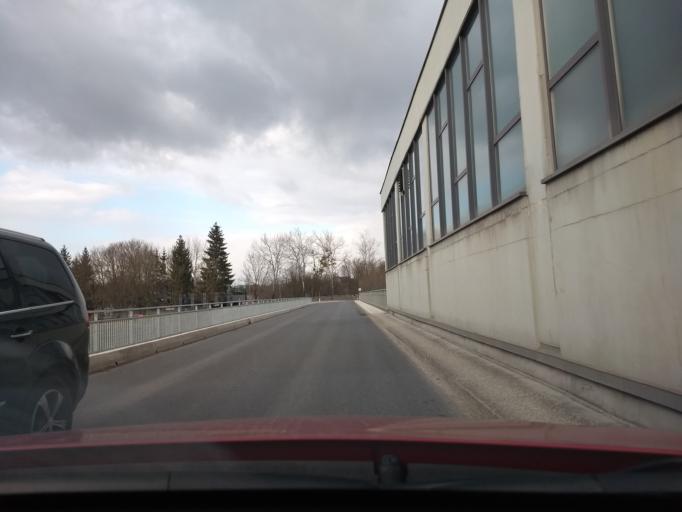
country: AT
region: Upper Austria
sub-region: Politischer Bezirk Steyr-Land
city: Garsten
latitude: 48.0180
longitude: 14.4117
